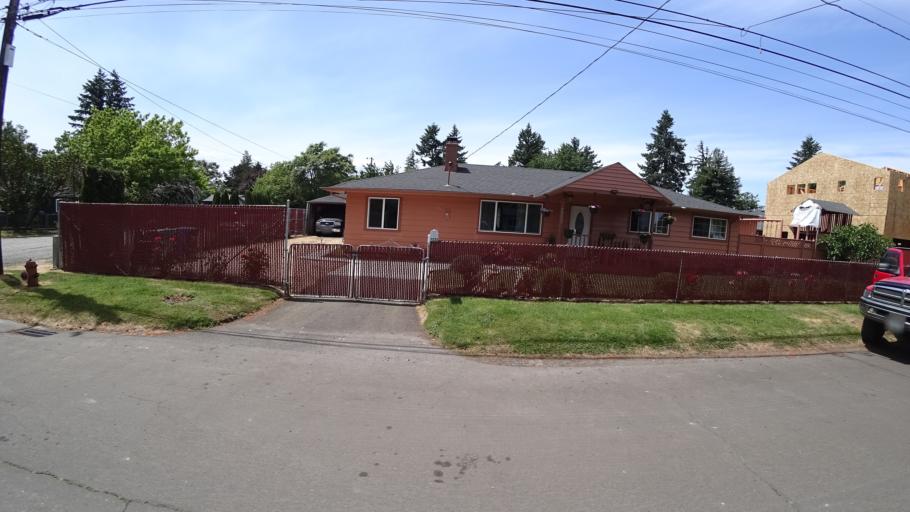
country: US
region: Oregon
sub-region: Multnomah County
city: Lents
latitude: 45.4705
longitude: -122.5981
